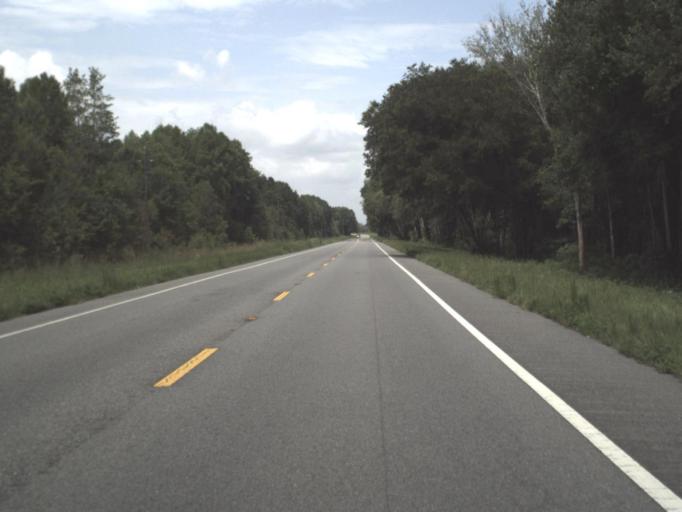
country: US
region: Florida
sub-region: Madison County
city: Madison
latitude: 30.4806
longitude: -83.5441
